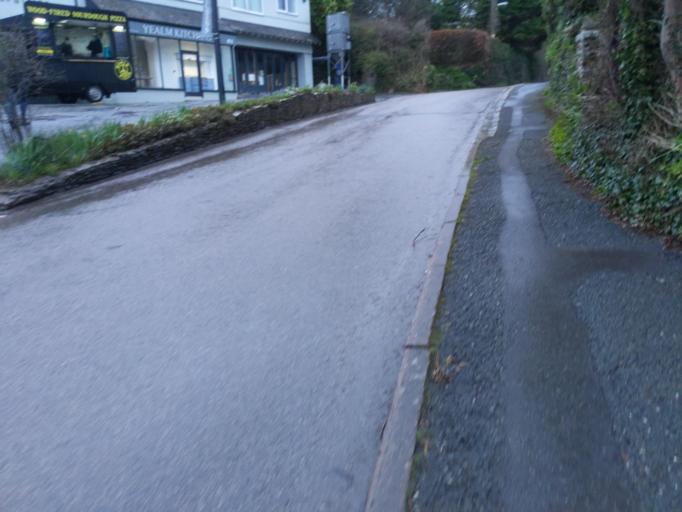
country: GB
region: England
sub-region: Devon
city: Wembury
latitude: 50.3177
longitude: -4.0359
